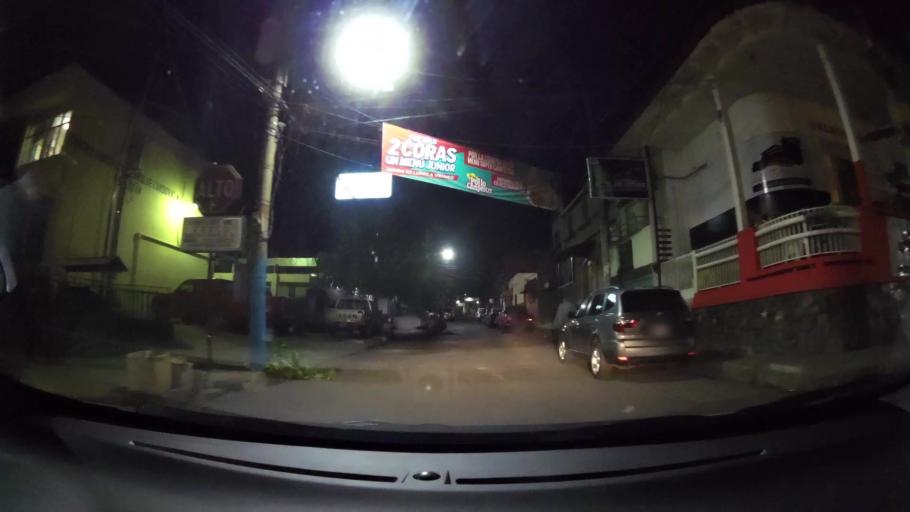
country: SV
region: Usulutan
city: Usulutan
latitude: 13.3454
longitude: -88.4399
